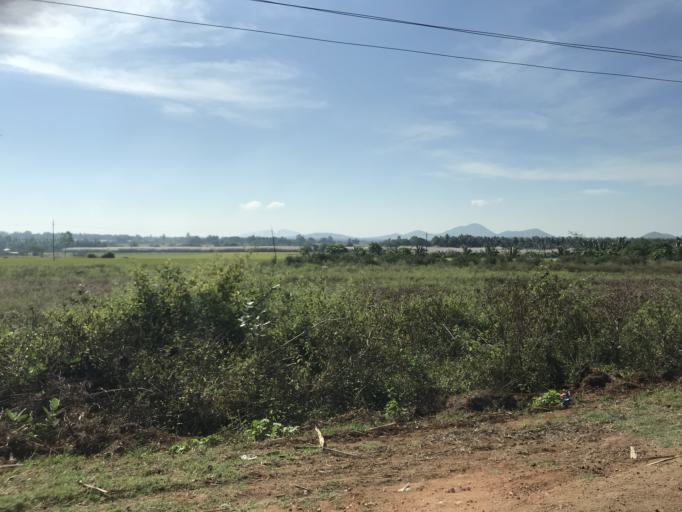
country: IN
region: Karnataka
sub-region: Mysore
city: Heggadadevankote
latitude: 12.1192
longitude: 76.4211
